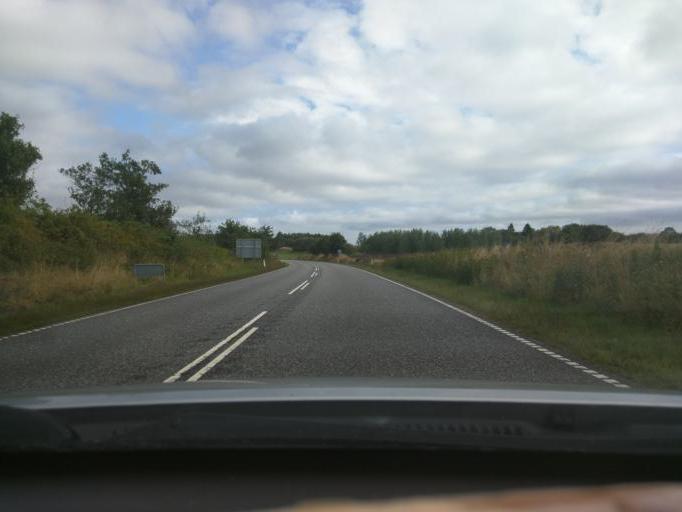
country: DK
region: Central Jutland
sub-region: Viborg Kommune
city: Viborg
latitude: 56.3593
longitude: 9.3664
